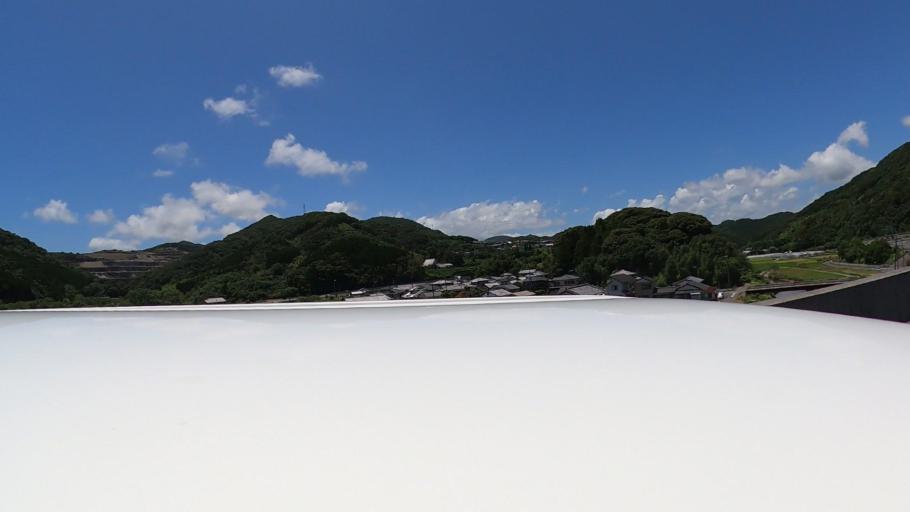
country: JP
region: Miyazaki
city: Nobeoka
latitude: 32.3987
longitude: 131.6179
